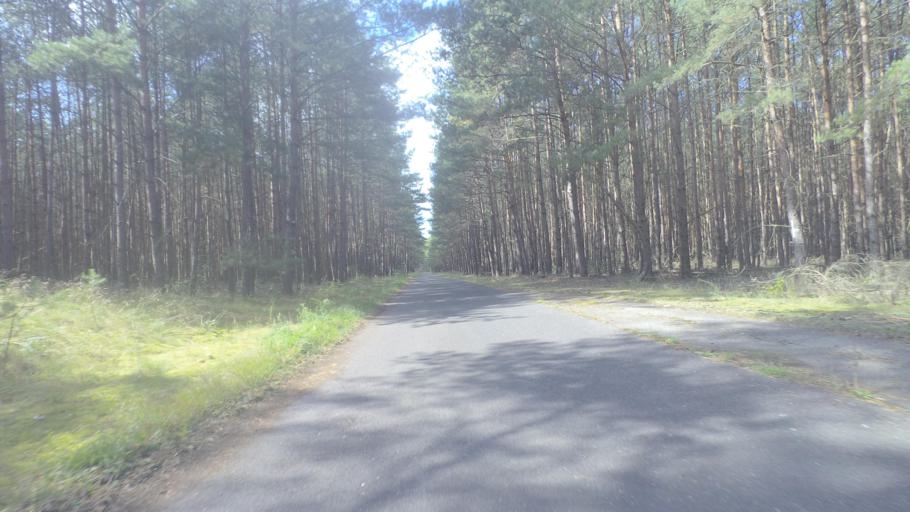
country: DE
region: Brandenburg
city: Munchehofe
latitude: 52.1728
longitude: 13.8783
